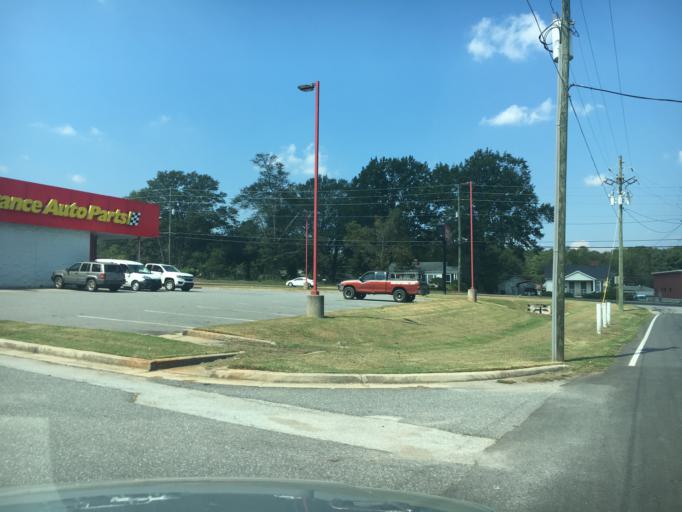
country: US
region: Georgia
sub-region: Hart County
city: Hartwell
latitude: 34.3533
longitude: -82.9191
